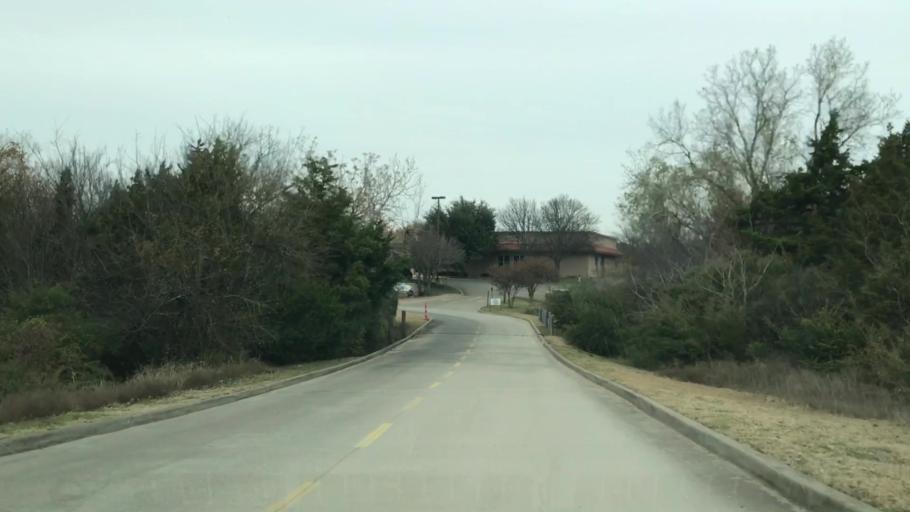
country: US
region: Texas
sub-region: Dallas County
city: Cockrell Hill
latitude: 32.7431
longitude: -96.8944
